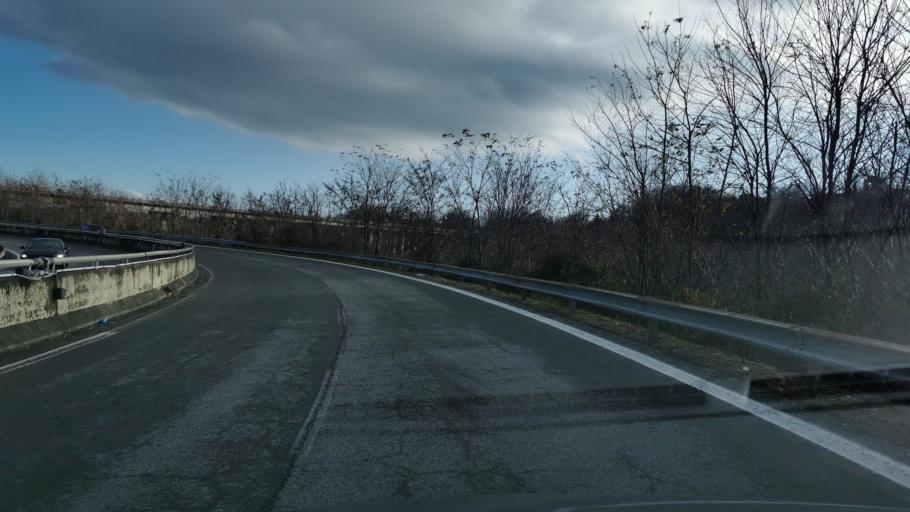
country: IT
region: Piedmont
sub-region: Provincia di Biella
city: Biella
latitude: 45.5622
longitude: 8.0706
